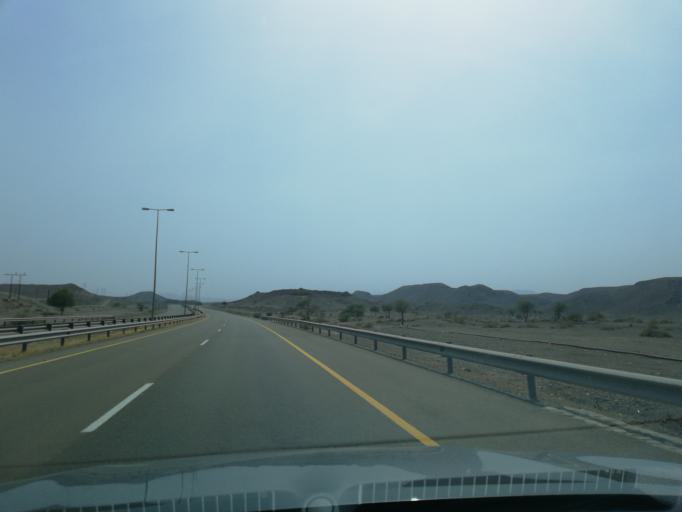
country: OM
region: Al Batinah
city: Al Liwa'
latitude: 24.3235
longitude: 56.4728
